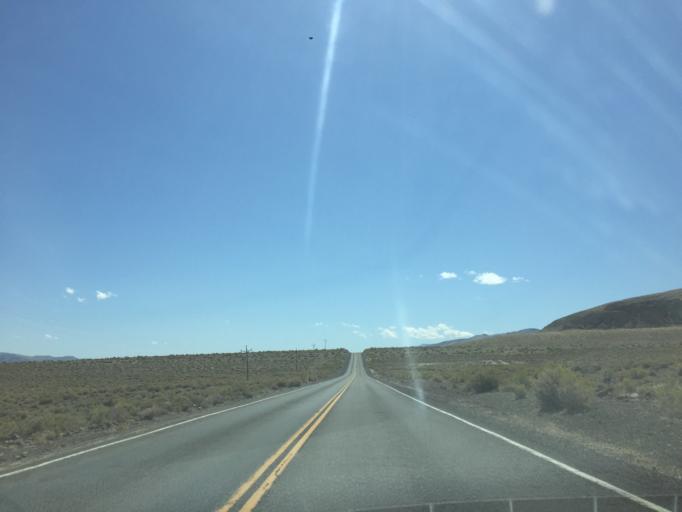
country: US
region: Nevada
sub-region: Lyon County
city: Fernley
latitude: 40.0913
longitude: -119.3719
